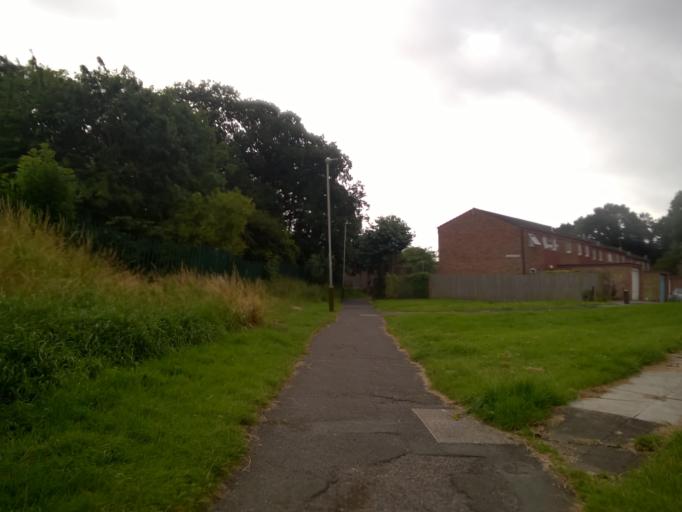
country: GB
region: England
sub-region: Leicestershire
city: Anstey
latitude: 52.6609
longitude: -1.1612
